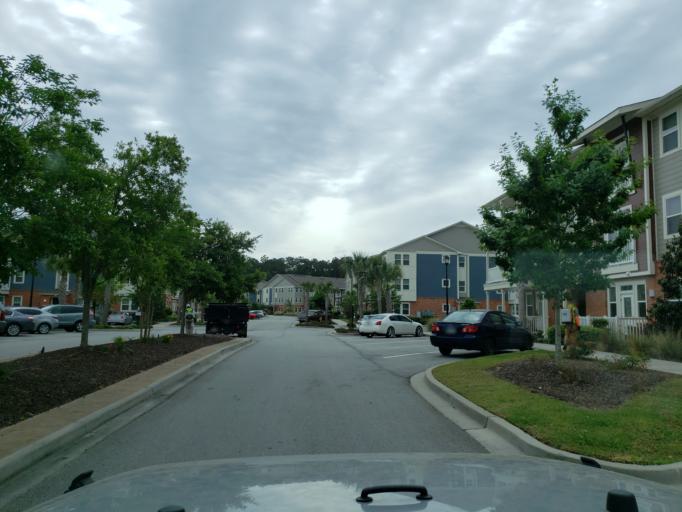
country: US
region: Georgia
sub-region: Chatham County
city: Pooler
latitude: 32.1750
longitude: -81.2309
